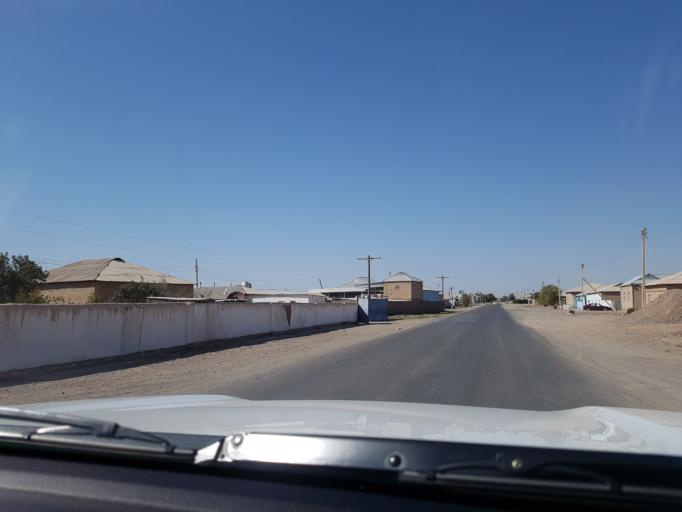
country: IR
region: Razavi Khorasan
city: Sarakhs
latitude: 36.5149
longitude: 61.2219
